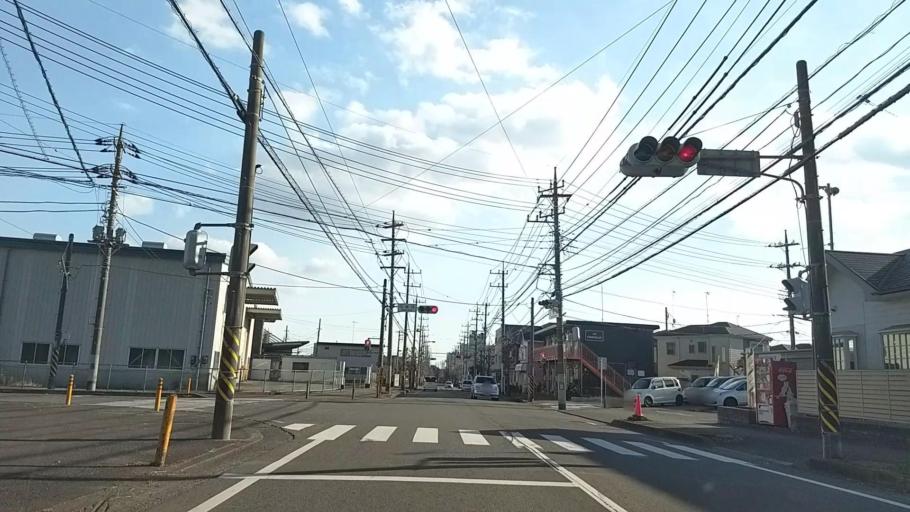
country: JP
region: Kanagawa
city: Atsugi
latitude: 35.4581
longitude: 139.3257
